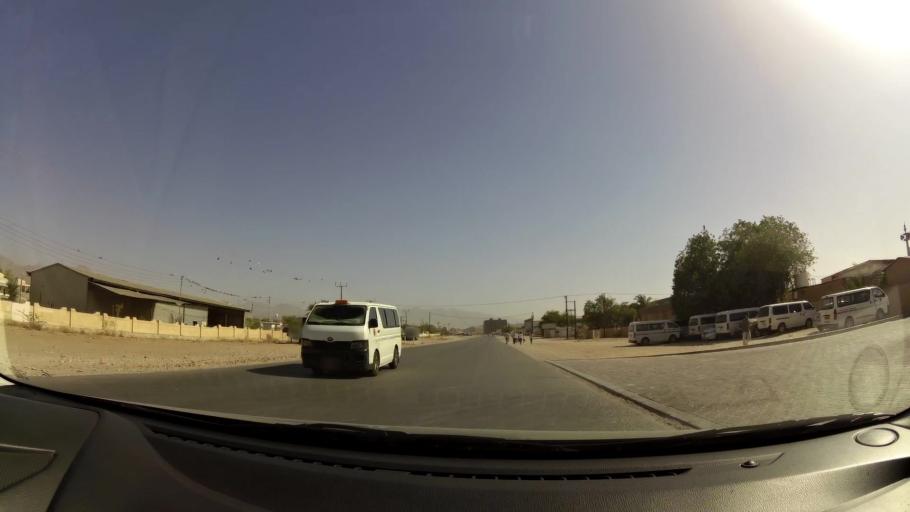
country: OM
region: Muhafazat Masqat
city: Bawshar
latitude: 23.5732
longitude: 58.3517
